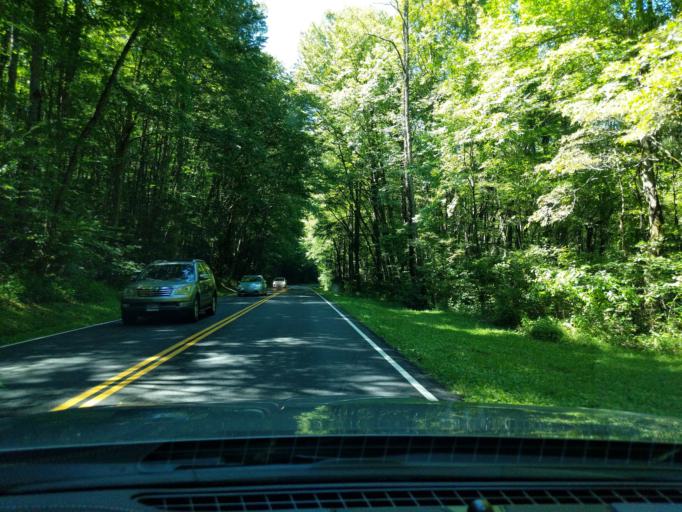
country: US
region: North Carolina
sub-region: Swain County
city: Cherokee
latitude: 35.5759
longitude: -83.3423
